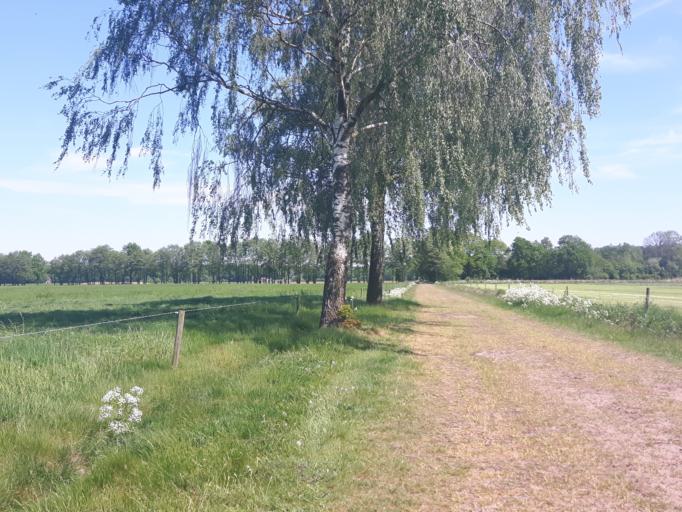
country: NL
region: Overijssel
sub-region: Gemeente Enschede
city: Enschede
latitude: 52.1697
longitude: 6.8597
